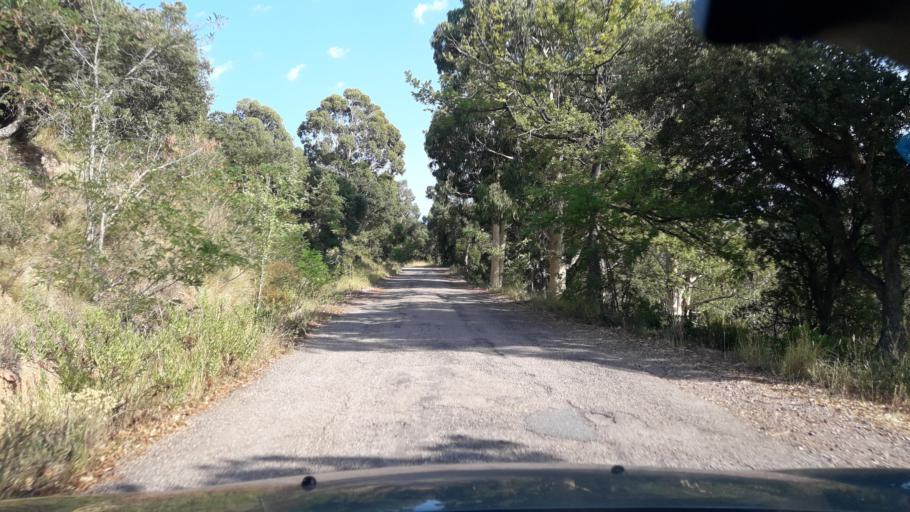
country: FR
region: Provence-Alpes-Cote d'Azur
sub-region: Departement du Var
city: Saint-Raphael
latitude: 43.4998
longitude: 6.7981
